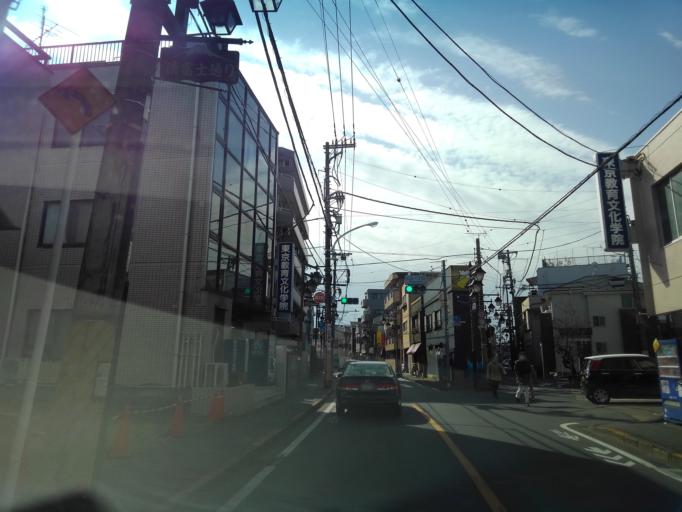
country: JP
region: Tokyo
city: Tanashicho
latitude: 35.7685
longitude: 139.5162
